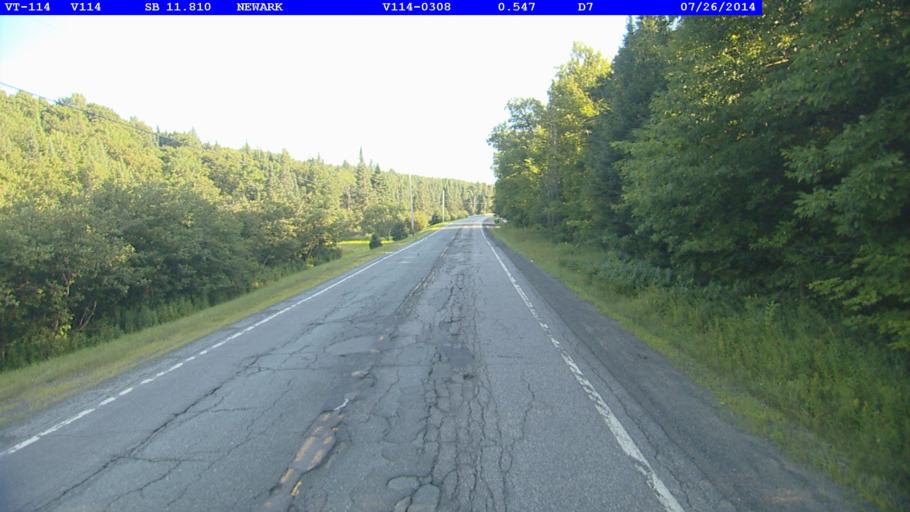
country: US
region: Vermont
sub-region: Caledonia County
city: Lyndonville
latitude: 44.6770
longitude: -71.8809
